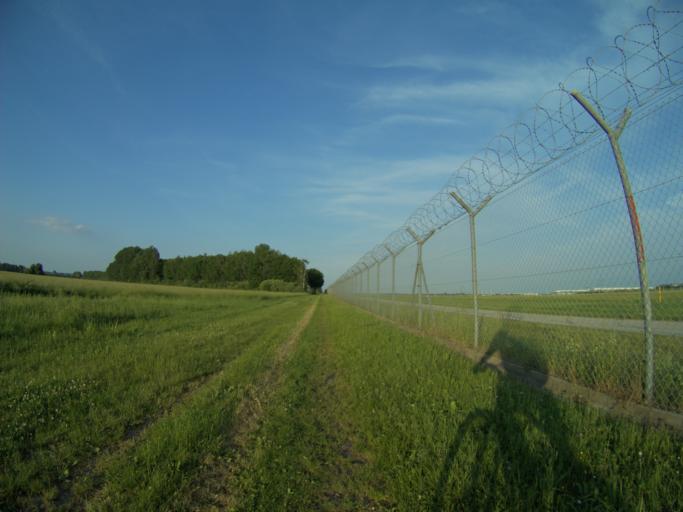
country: DE
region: Bavaria
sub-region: Upper Bavaria
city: Marzling
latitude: 48.3662
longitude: 11.7771
